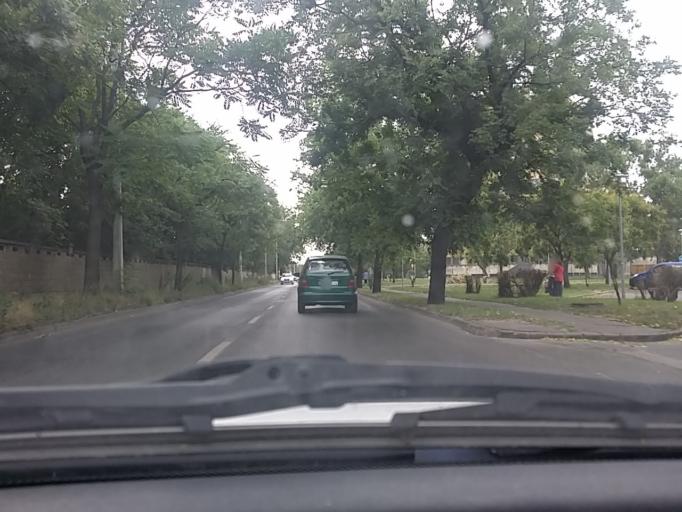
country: HU
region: Budapest
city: Budapest X. keruelet
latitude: 47.4848
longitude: 19.1254
